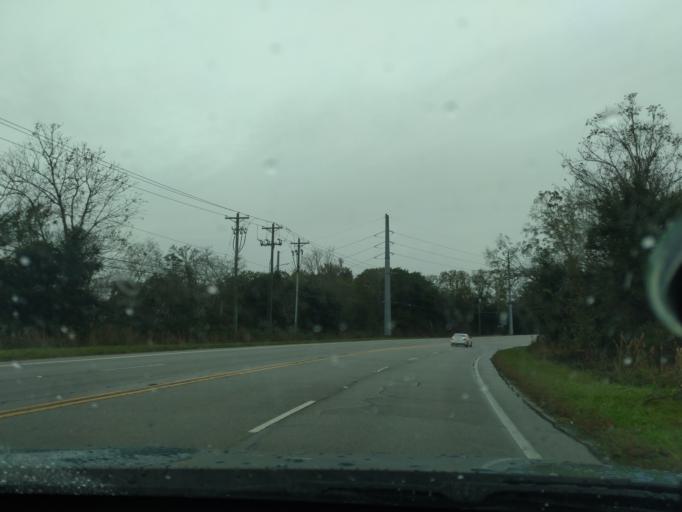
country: US
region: South Carolina
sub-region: Charleston County
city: Folly Beach
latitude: 32.6968
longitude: -79.9674
